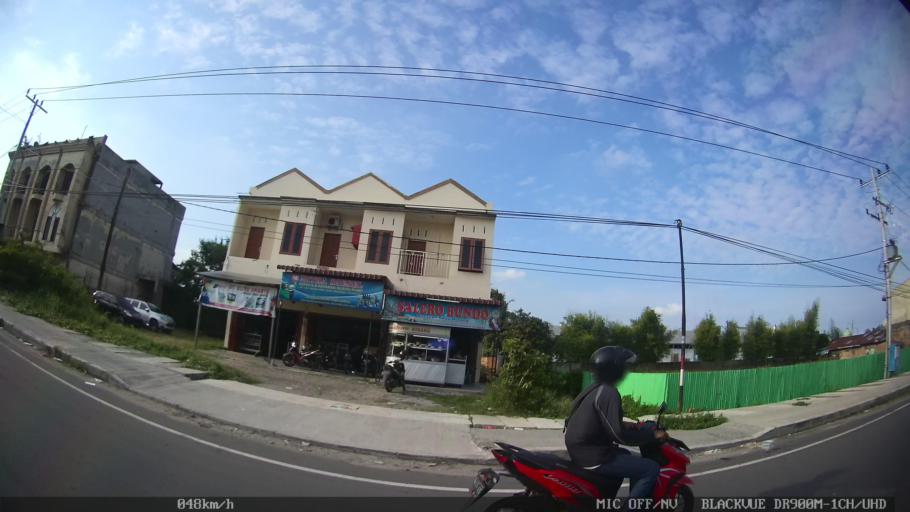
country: ID
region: North Sumatra
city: Medan
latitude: 3.6159
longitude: 98.6424
